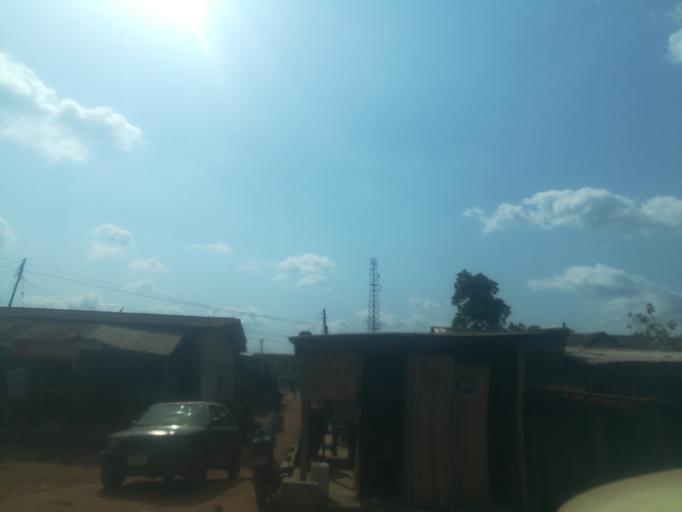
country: NG
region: Oyo
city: Moniya
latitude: 7.5300
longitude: 3.9114
